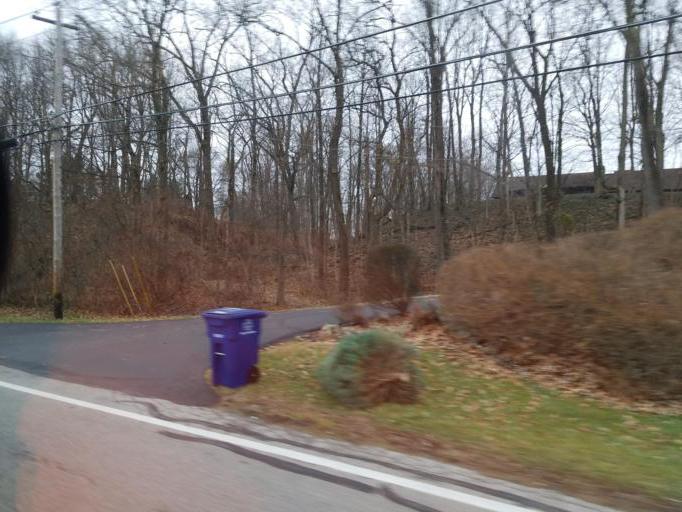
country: US
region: Ohio
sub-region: Franklin County
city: Minerva Park
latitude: 40.0921
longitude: -82.9357
